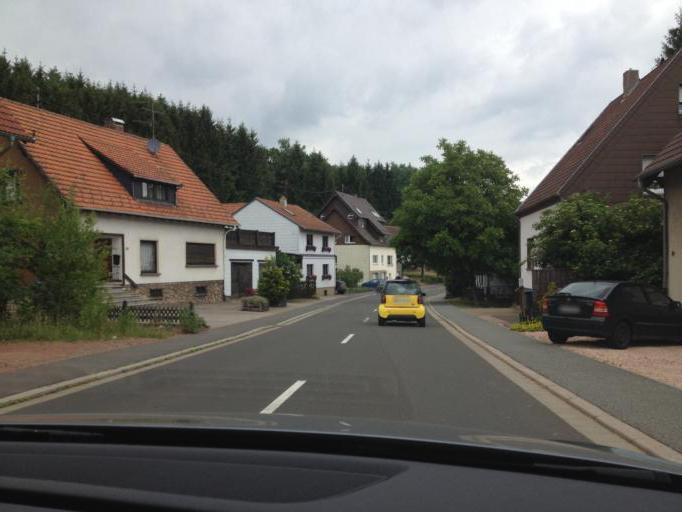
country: DE
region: Rheinland-Pfalz
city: Breitenbach
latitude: 49.4179
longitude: 7.2612
